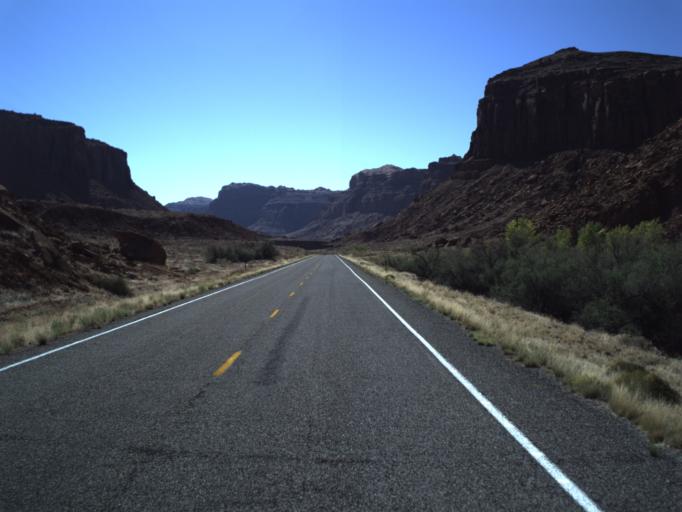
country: US
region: Utah
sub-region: San Juan County
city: Blanding
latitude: 37.9396
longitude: -110.4692
